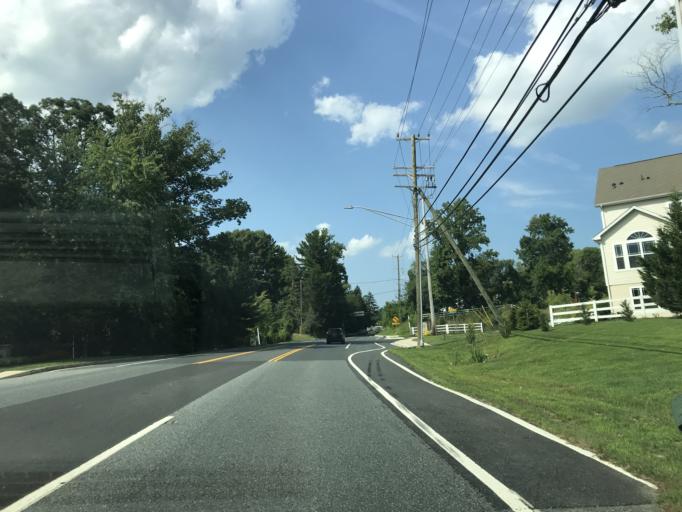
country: US
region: Maryland
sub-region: Harford County
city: South Bel Air
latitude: 39.5640
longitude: -76.3331
